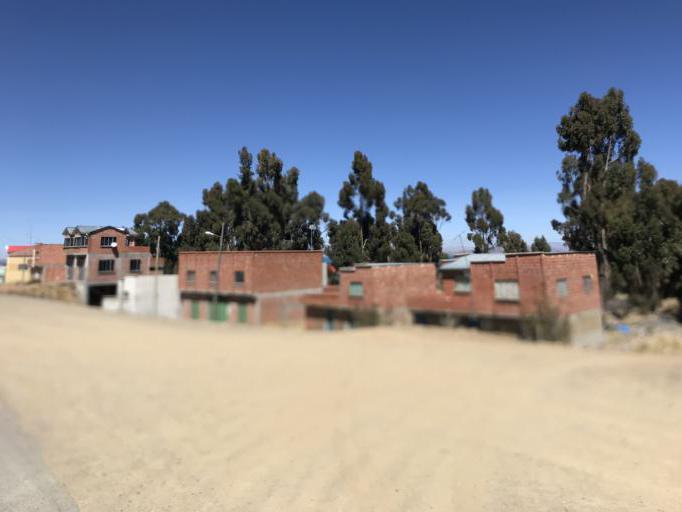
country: BO
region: La Paz
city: Huatajata
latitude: -16.1984
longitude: -68.7153
